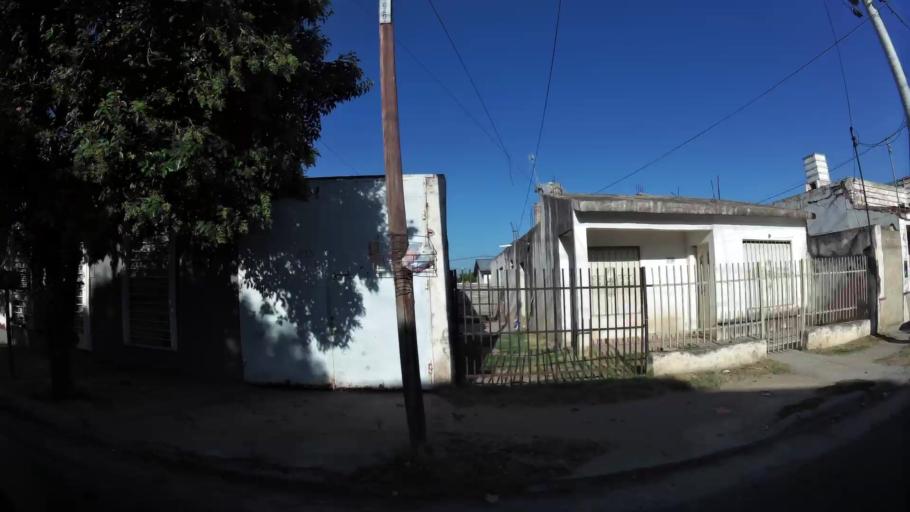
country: AR
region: Cordoba
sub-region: Departamento de Capital
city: Cordoba
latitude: -31.4403
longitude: -64.2481
